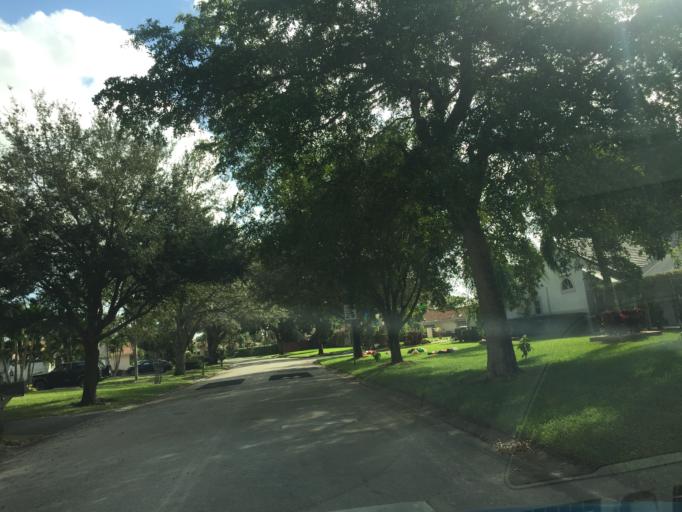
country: US
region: Florida
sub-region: Broward County
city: North Lauderdale
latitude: 26.2314
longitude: -80.2402
